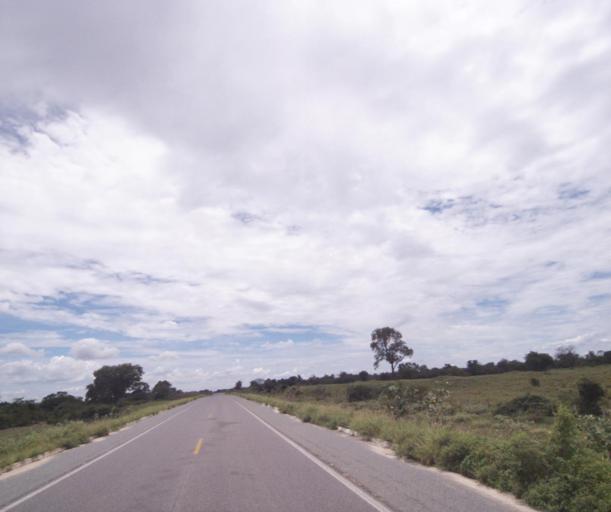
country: BR
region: Bahia
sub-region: Carinhanha
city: Carinhanha
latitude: -14.3080
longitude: -43.7852
